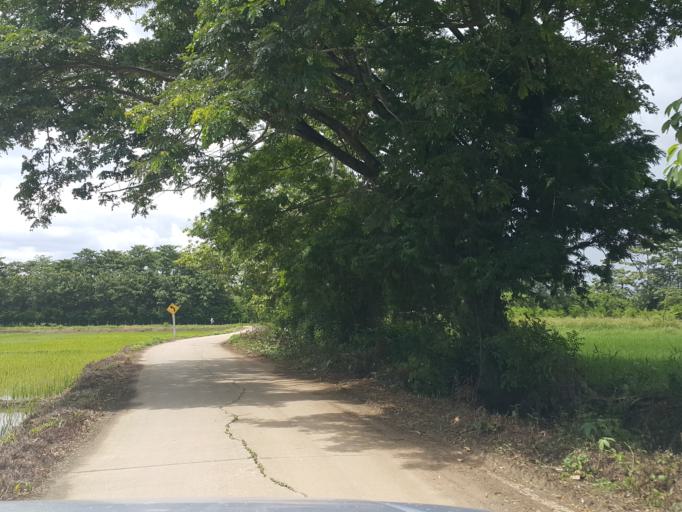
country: TH
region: Chiang Mai
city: San Kamphaeng
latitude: 18.7919
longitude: 99.1177
